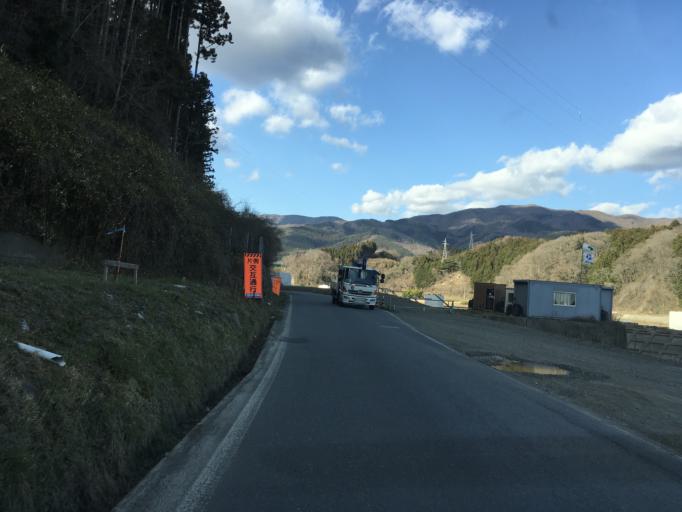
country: JP
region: Iwate
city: Ofunato
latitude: 39.0217
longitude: 141.6161
